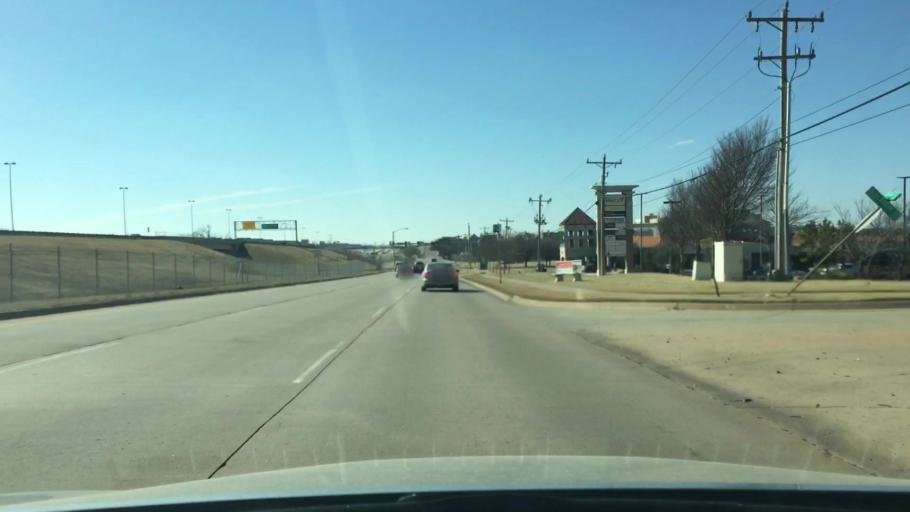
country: US
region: Oklahoma
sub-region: Oklahoma County
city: The Village
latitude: 35.6103
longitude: -97.6004
